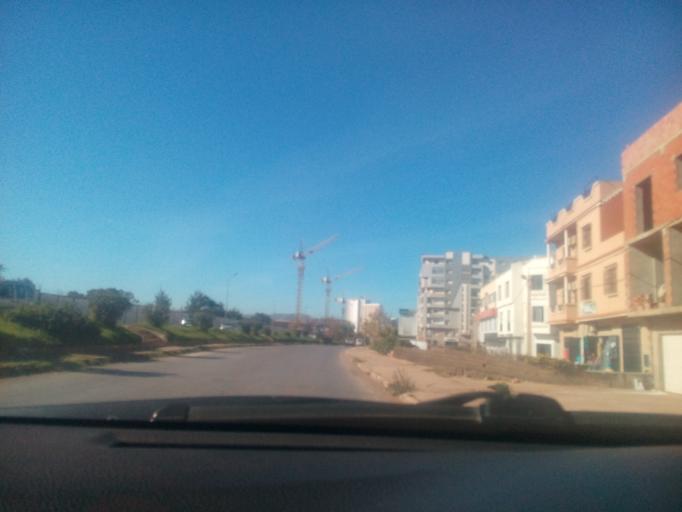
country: DZ
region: Oran
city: Bir el Djir
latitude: 35.7169
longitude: -0.5926
